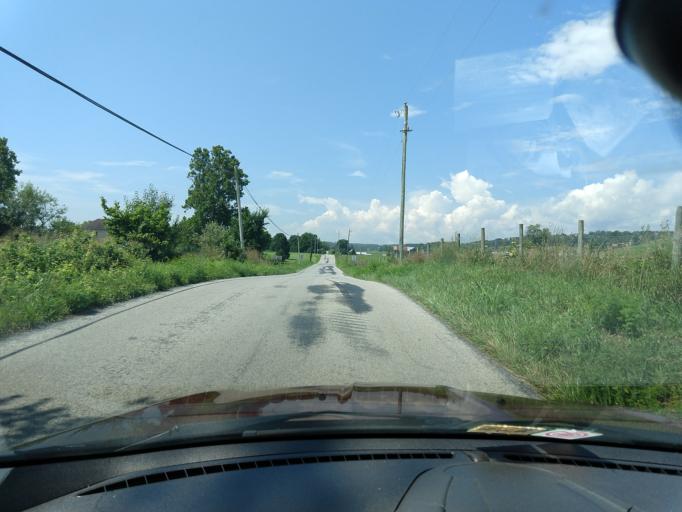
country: US
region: Virginia
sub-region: Rockingham County
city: Broadway
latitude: 38.6006
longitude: -78.8217
